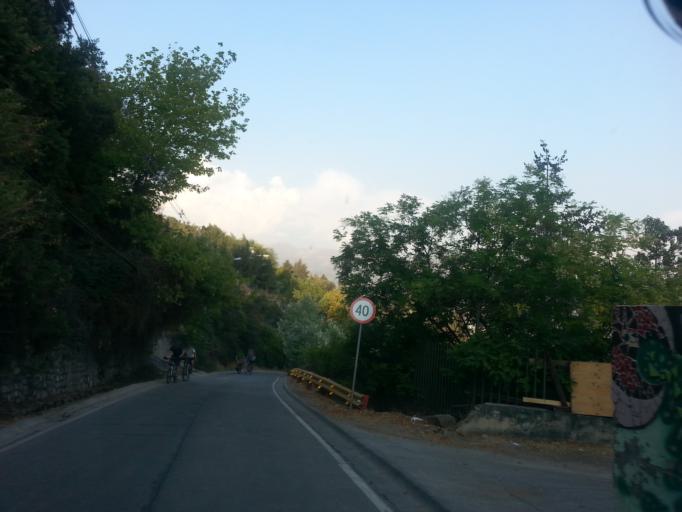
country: CL
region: Santiago Metropolitan
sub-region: Provincia de Santiago
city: Villa Presidente Frei, Nunoa, Santiago, Chile
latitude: -33.3638
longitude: -70.5566
